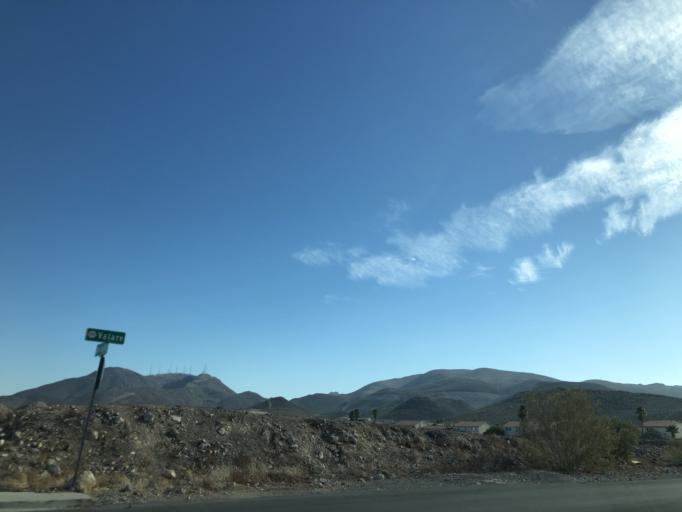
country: US
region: Nevada
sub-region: Clark County
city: Henderson
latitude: 36.0218
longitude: -115.0422
